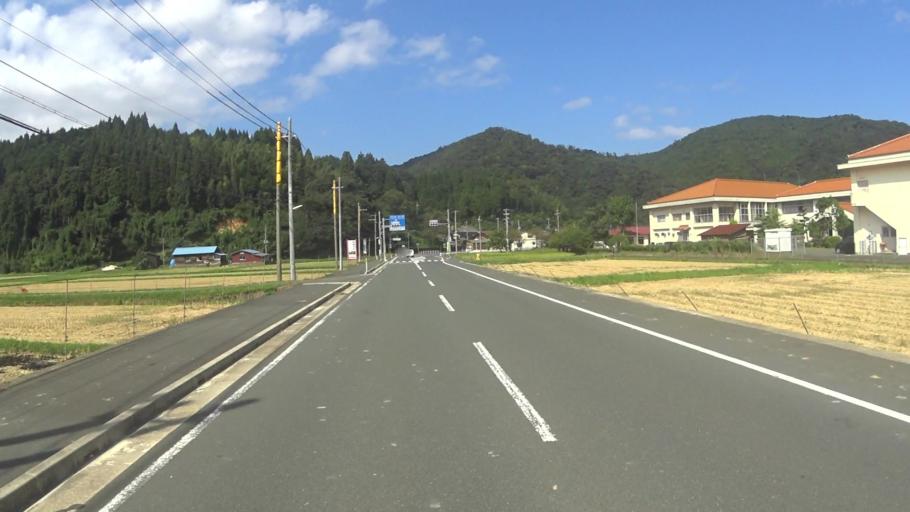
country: JP
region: Kyoto
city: Miyazu
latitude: 35.7280
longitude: 135.2554
